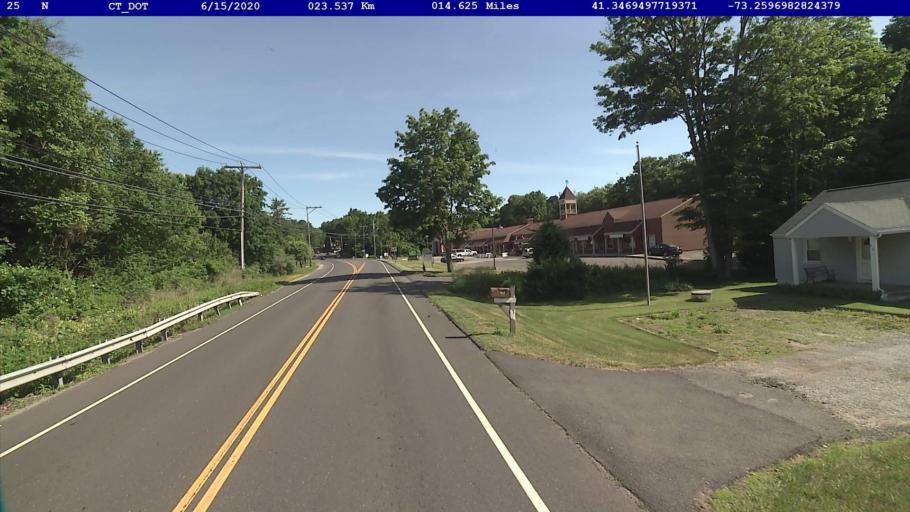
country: US
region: Connecticut
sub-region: Fairfield County
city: Newtown
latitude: 41.3470
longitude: -73.2597
